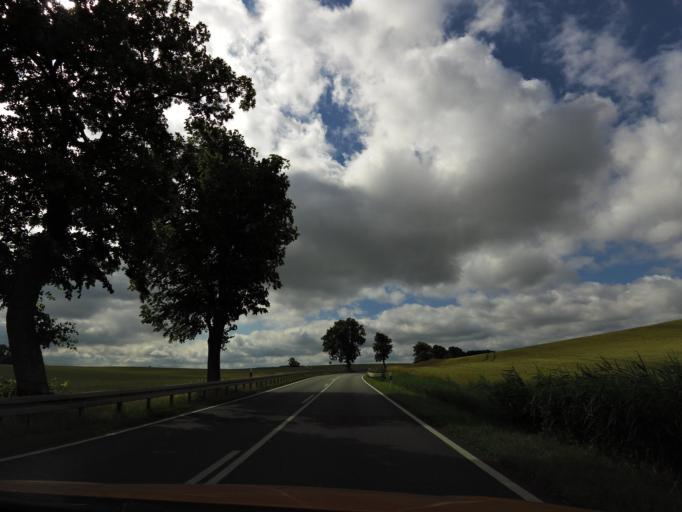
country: DE
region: Mecklenburg-Vorpommern
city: Krakow am See
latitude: 53.7056
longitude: 12.2783
